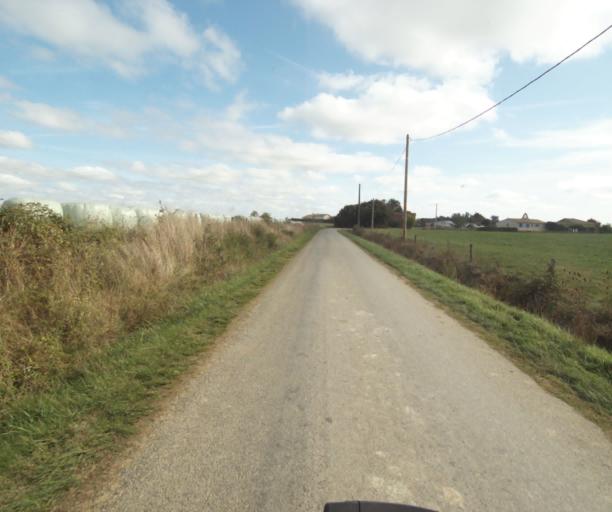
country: FR
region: Midi-Pyrenees
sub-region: Departement du Tarn-et-Garonne
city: Saint-Porquier
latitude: 43.9597
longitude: 1.1491
